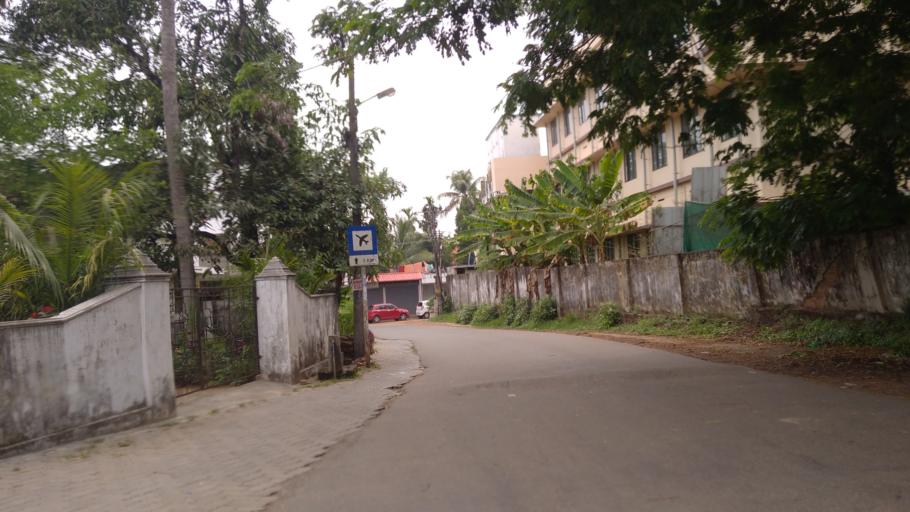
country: IN
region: Kerala
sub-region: Ernakulam
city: Angamali
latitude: 10.1685
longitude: 76.3984
